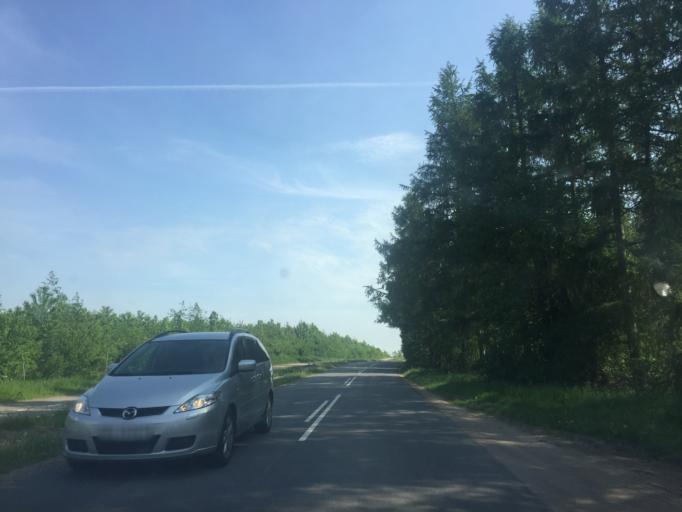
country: DK
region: Capital Region
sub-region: Egedal Kommune
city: Smorumnedre
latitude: 55.7247
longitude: 12.2914
